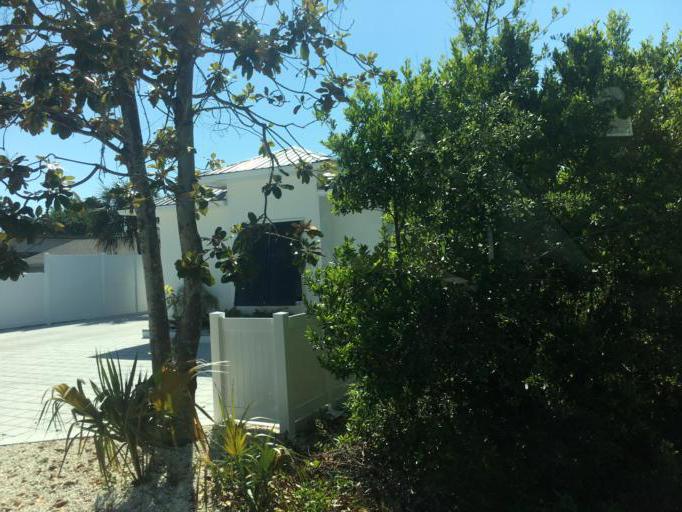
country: US
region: Florida
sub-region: Bay County
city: Panama City Beach
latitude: 30.2046
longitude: -85.8463
